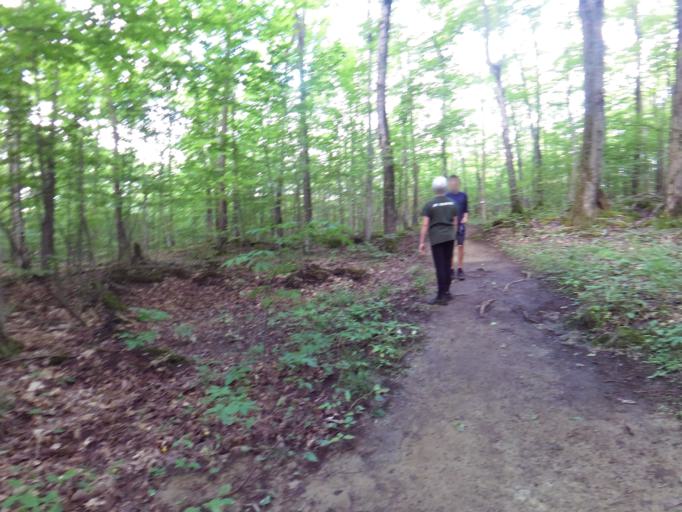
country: CA
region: Ontario
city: Owen Sound
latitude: 44.9539
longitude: -81.1439
